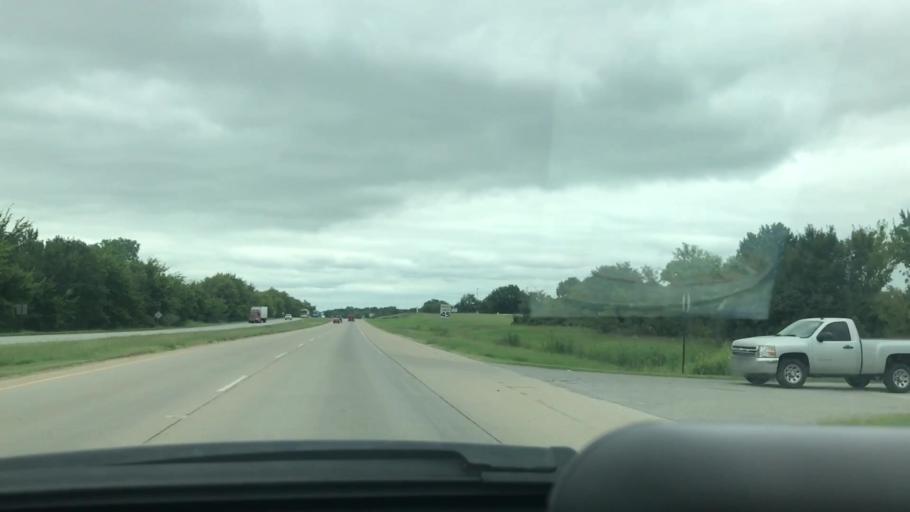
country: US
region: Oklahoma
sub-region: Mayes County
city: Chouteau
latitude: 36.1920
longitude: -95.3420
